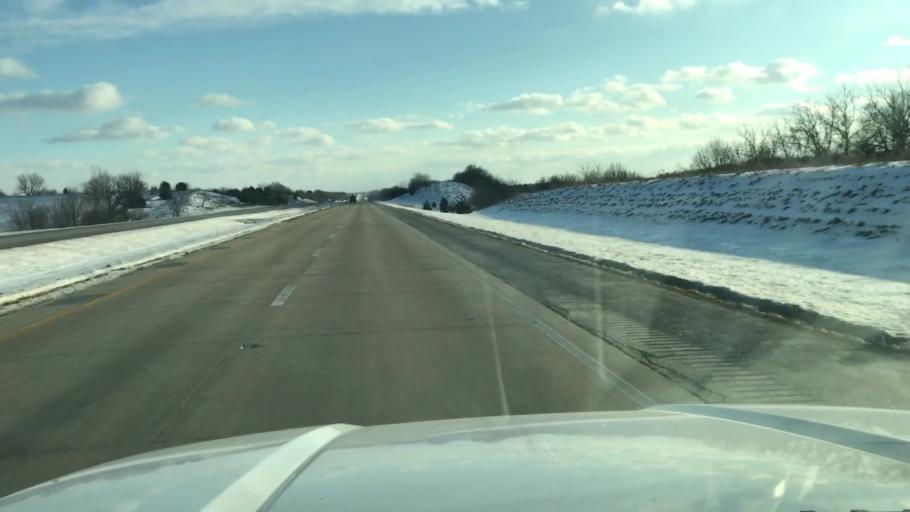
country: US
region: Missouri
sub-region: Andrew County
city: Savannah
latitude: 39.9527
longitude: -94.8604
